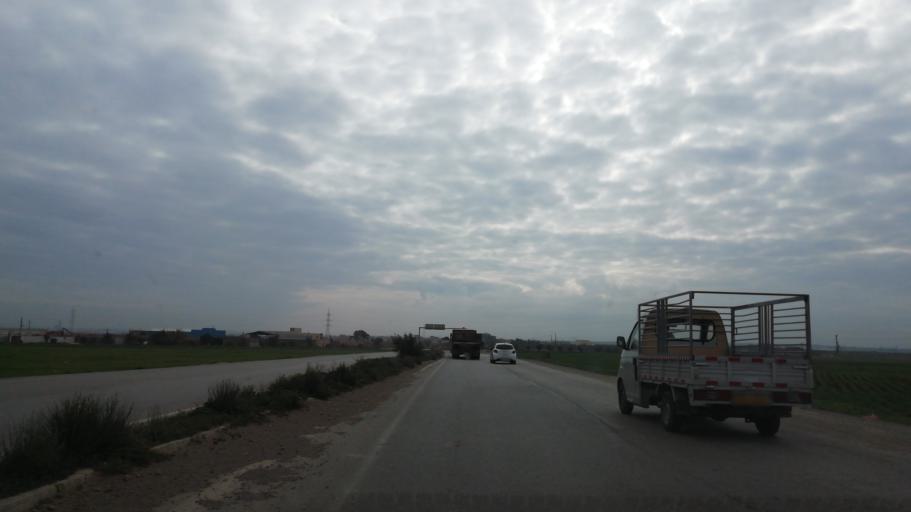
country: DZ
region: Oran
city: Ain el Bya
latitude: 35.7959
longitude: -0.3439
